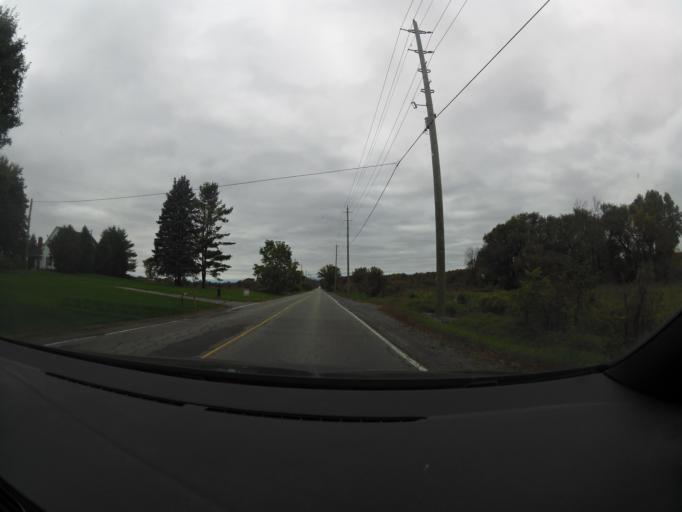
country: CA
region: Ontario
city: Bells Corners
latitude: 45.3186
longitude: -75.9575
